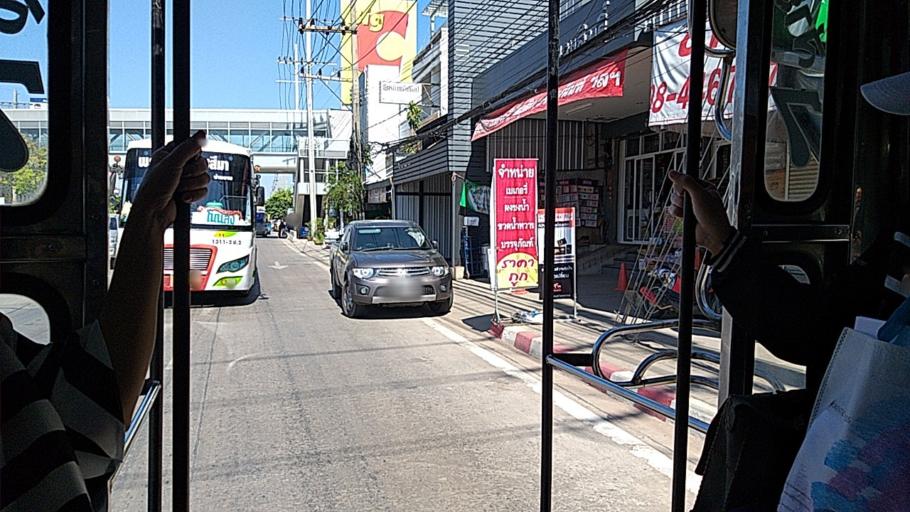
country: TH
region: Nakhon Ratchasima
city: Nakhon Ratchasima
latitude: 14.9808
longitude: 102.0905
